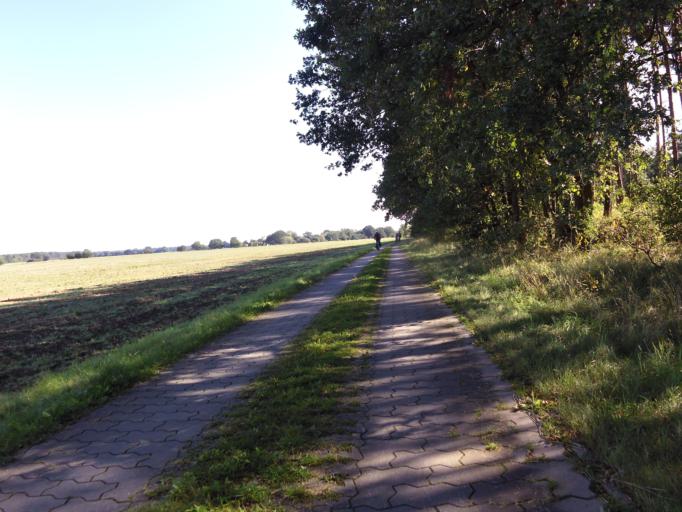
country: DE
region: Saxony-Anhalt
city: Rodleben
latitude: 51.8506
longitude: 12.1638
